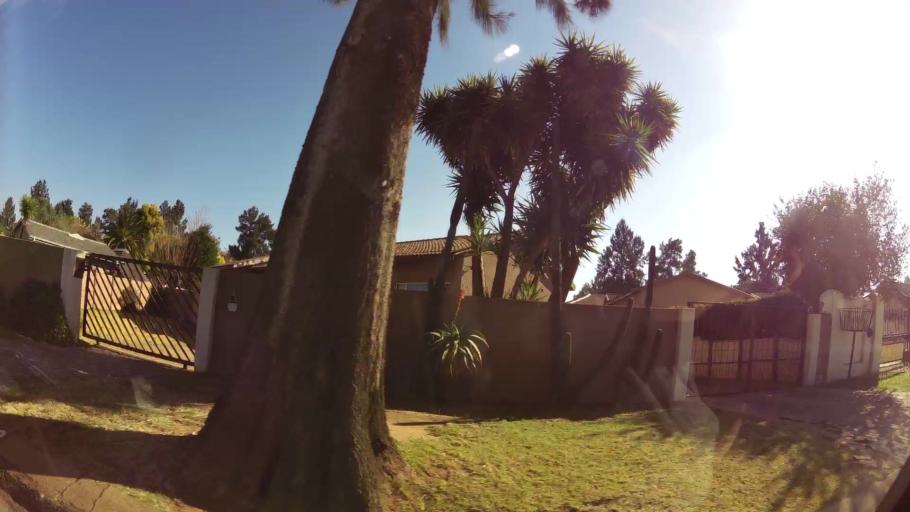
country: ZA
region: Gauteng
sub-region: Ekurhuleni Metropolitan Municipality
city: Germiston
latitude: -26.3399
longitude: 28.1015
